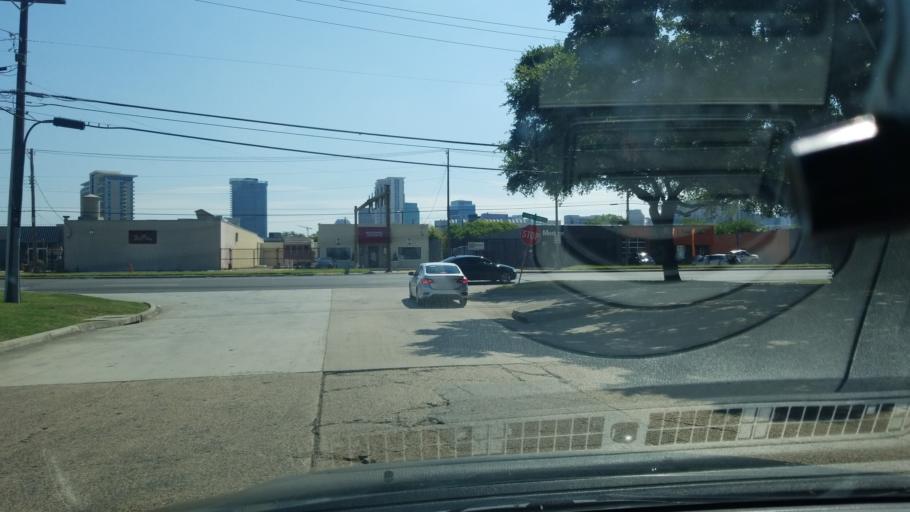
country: US
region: Texas
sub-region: Dallas County
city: Dallas
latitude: 32.7905
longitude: -96.8215
